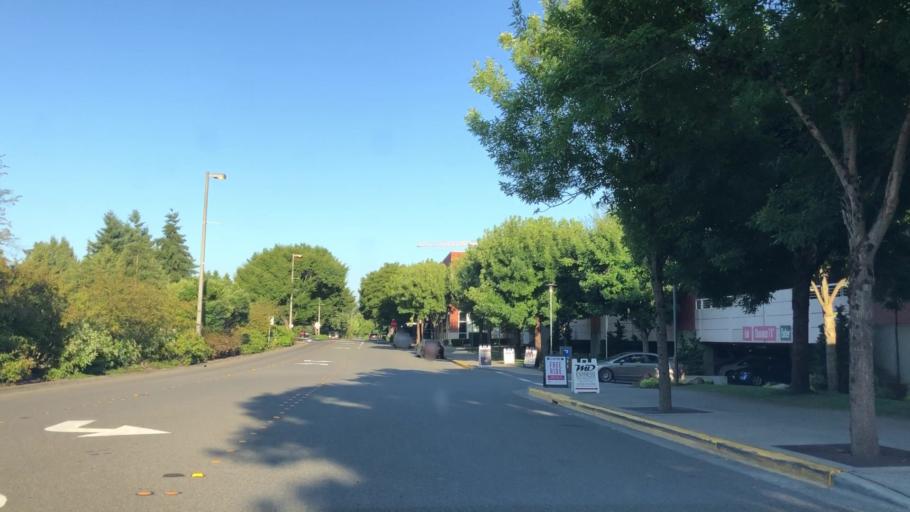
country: US
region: Washington
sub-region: King County
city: Redmond
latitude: 47.6720
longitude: -122.1206
